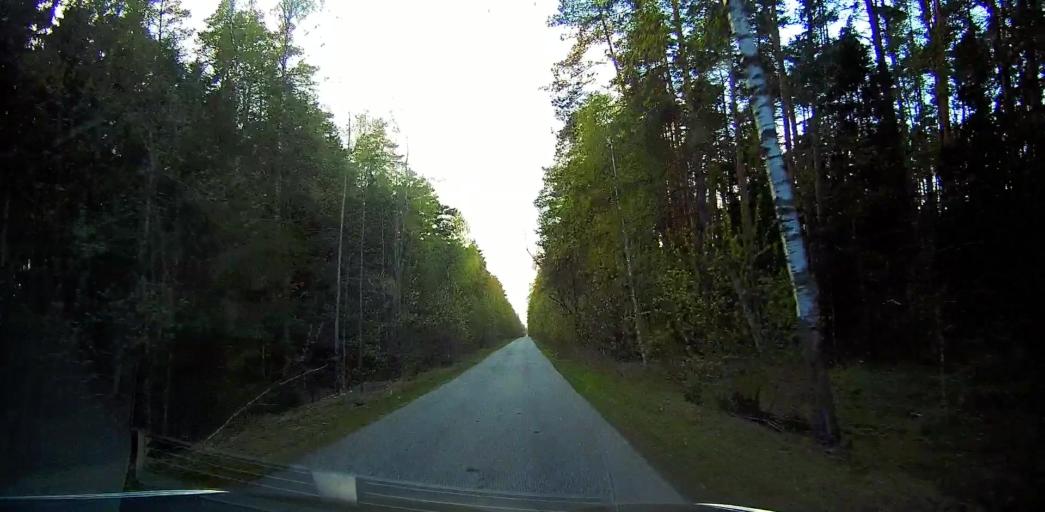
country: RU
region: Moskovskaya
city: Malyshevo
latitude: 55.5454
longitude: 38.3757
